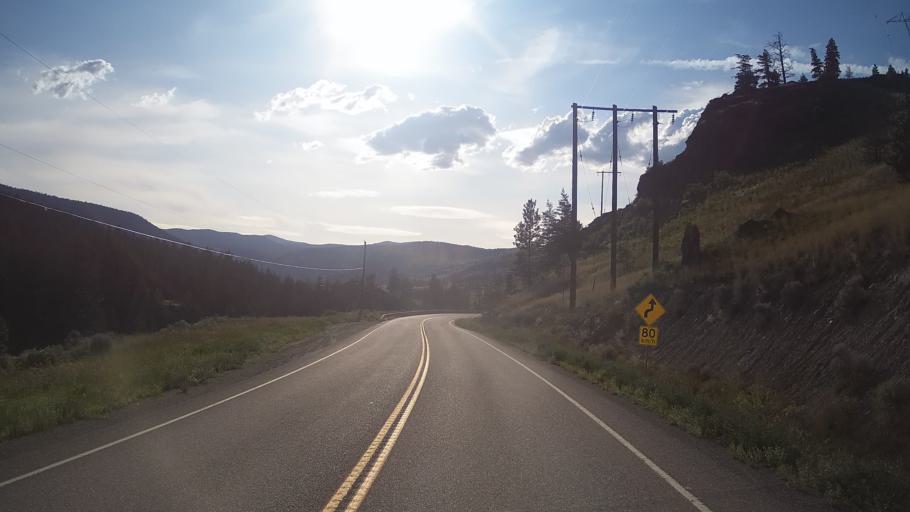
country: CA
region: British Columbia
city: Cache Creek
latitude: 50.8859
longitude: -121.4347
